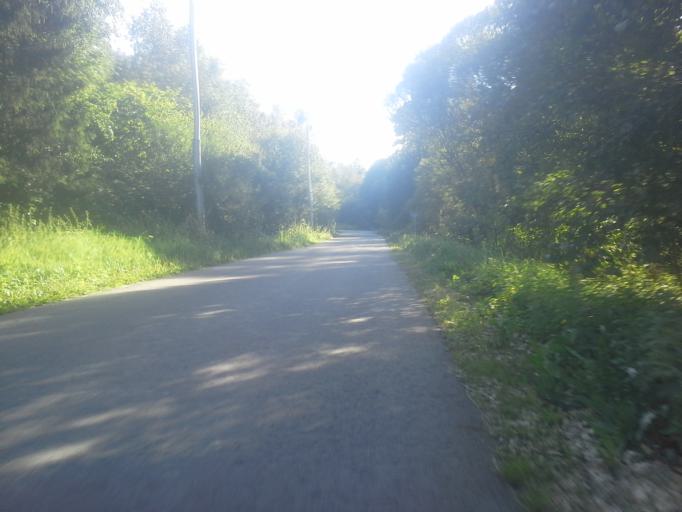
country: RU
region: Moskovskaya
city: Kievskij
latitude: 55.3465
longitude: 36.9426
